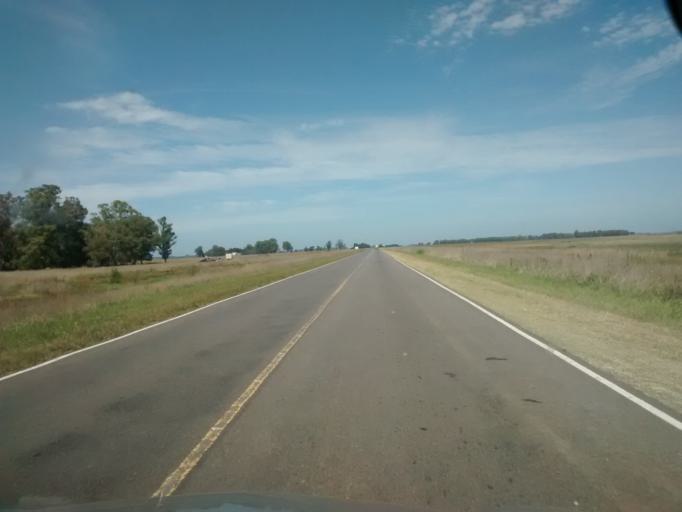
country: AR
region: Buenos Aires
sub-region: Partido de Rauch
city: Rauch
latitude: -36.5778
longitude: -58.5637
